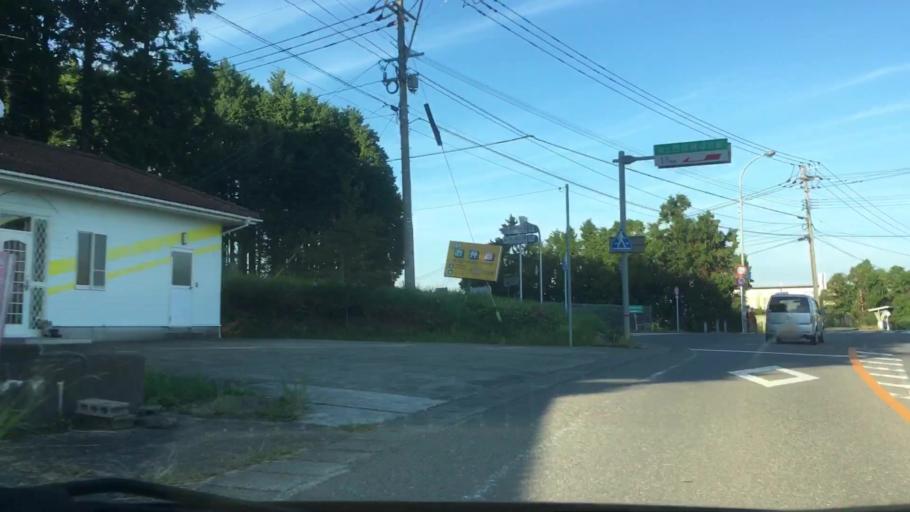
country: JP
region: Nagasaki
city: Sasebo
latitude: 33.0445
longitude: 129.6957
